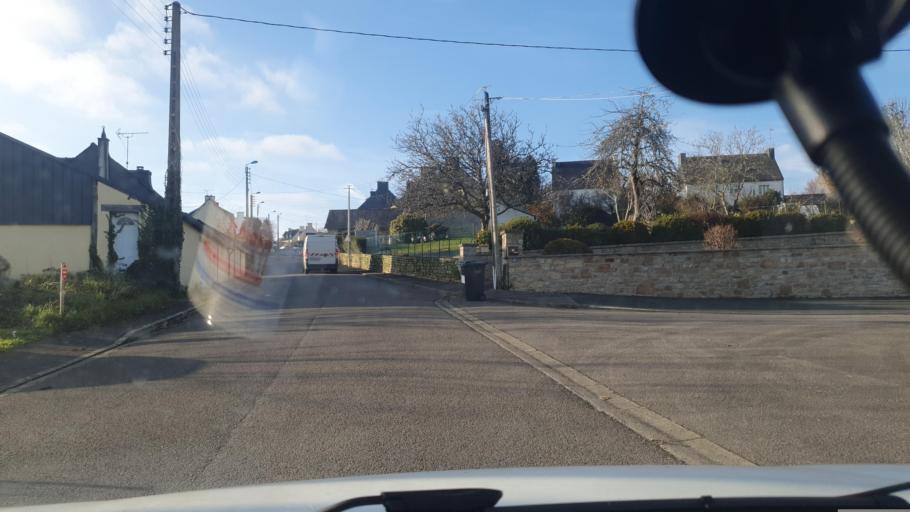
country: FR
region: Brittany
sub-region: Departement du Finistere
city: Edern
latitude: 48.1012
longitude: -3.9887
